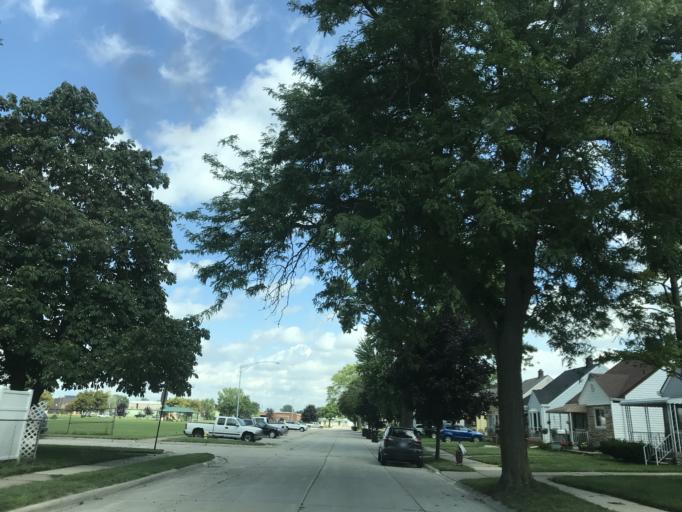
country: US
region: Michigan
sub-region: Wayne County
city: Riverview
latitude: 42.1678
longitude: -83.1770
